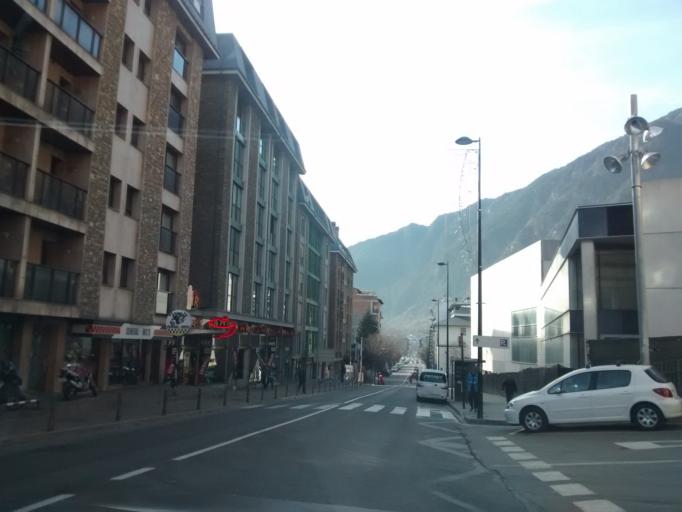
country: AD
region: Andorra la Vella
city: Andorra la Vella
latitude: 42.5010
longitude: 1.5101
